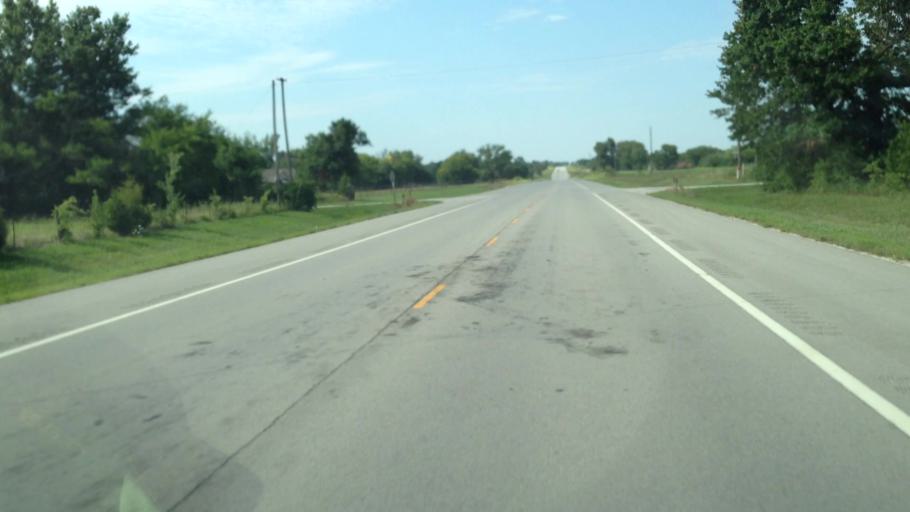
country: US
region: Kansas
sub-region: Labette County
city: Parsons
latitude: 37.2660
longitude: -95.2672
